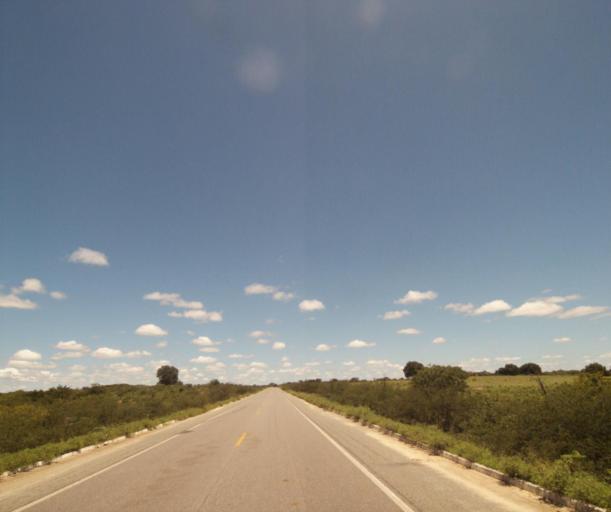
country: BR
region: Bahia
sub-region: Carinhanha
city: Carinhanha
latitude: -14.2961
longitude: -43.7855
